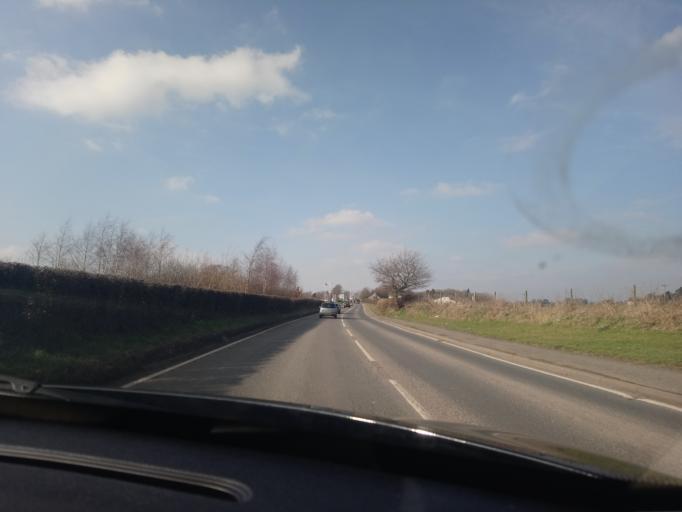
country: GB
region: England
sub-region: Shropshire
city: Berrington
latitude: 52.6895
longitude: -2.7051
